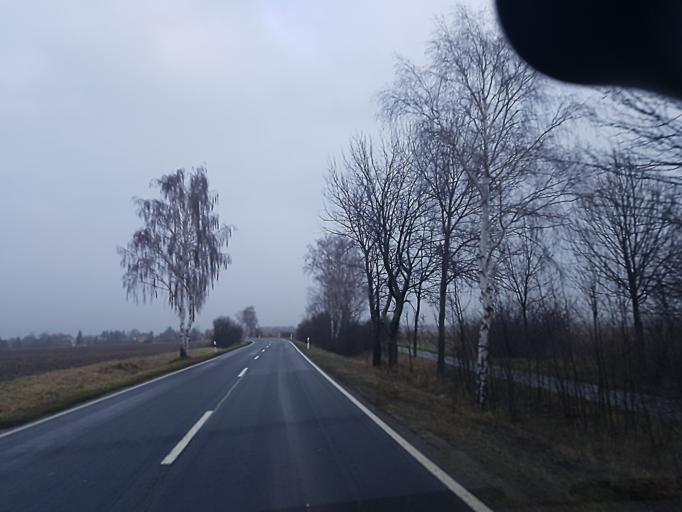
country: DE
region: Brandenburg
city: Finsterwalde
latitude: 51.6034
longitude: 13.7140
